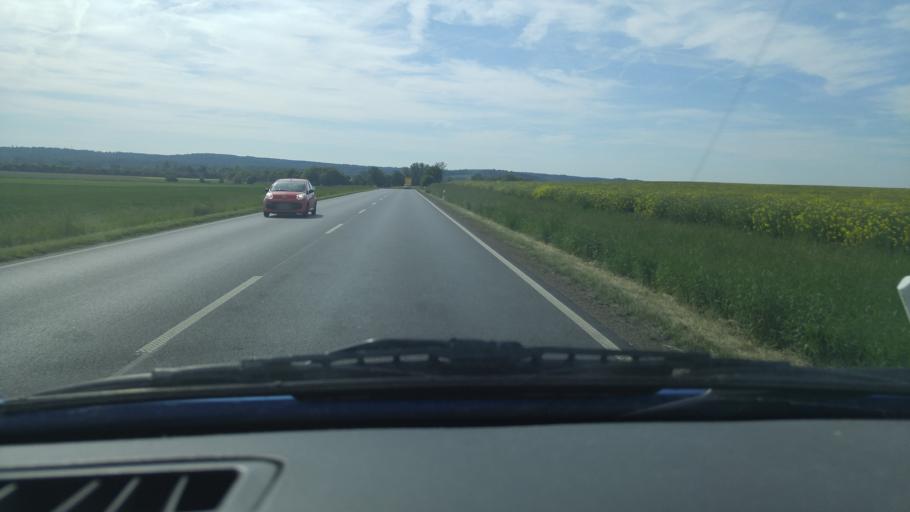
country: DE
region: Hesse
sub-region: Regierungsbezirk Darmstadt
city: Echzell
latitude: 50.4198
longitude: 8.8869
